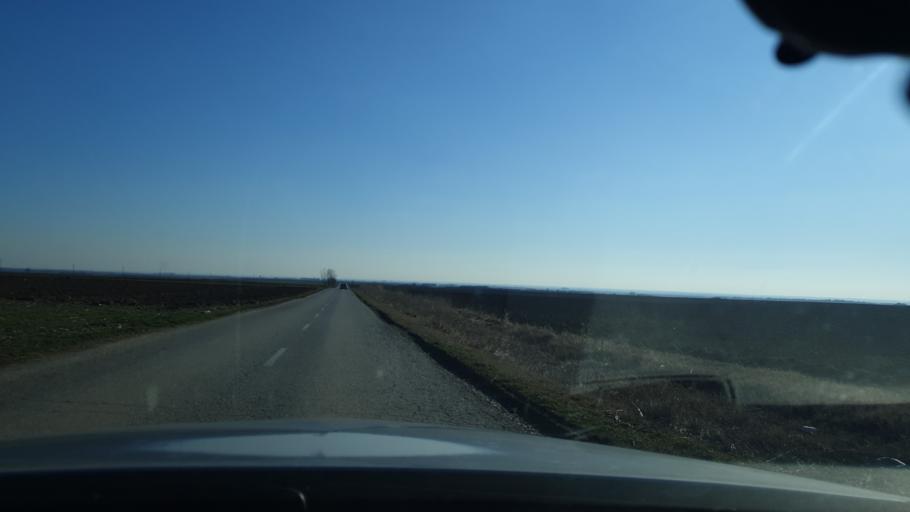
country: RS
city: Vrdnik
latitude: 45.0826
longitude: 19.8074
